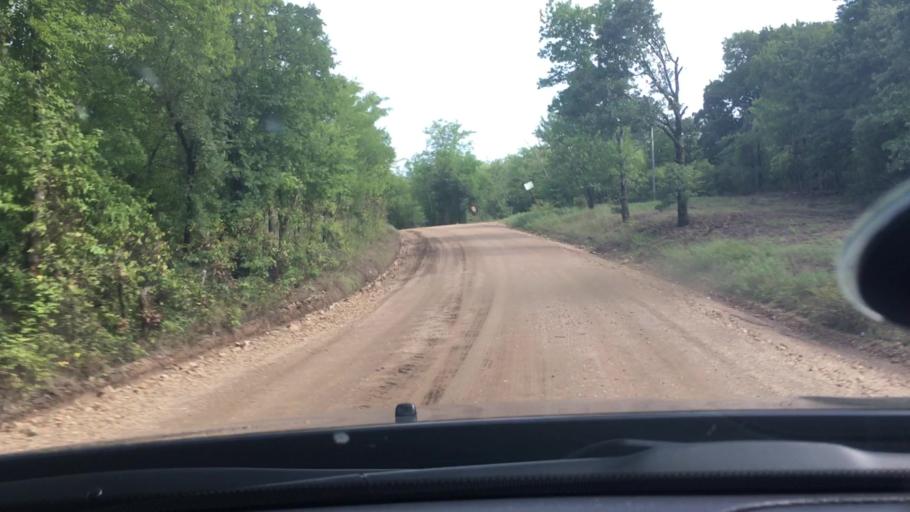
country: US
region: Oklahoma
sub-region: Atoka County
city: Atoka
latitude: 34.4455
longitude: -96.0670
